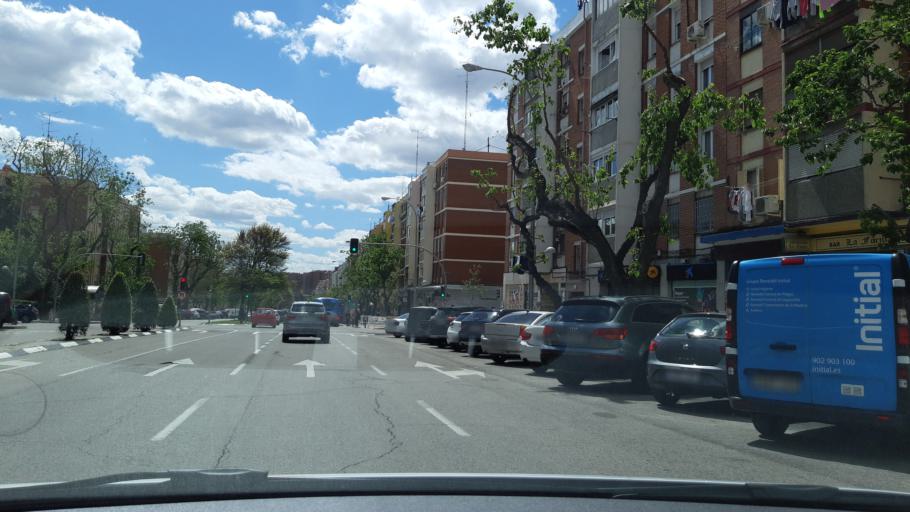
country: ES
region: Madrid
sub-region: Provincia de Madrid
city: Moratalaz
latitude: 40.4264
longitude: -3.6511
